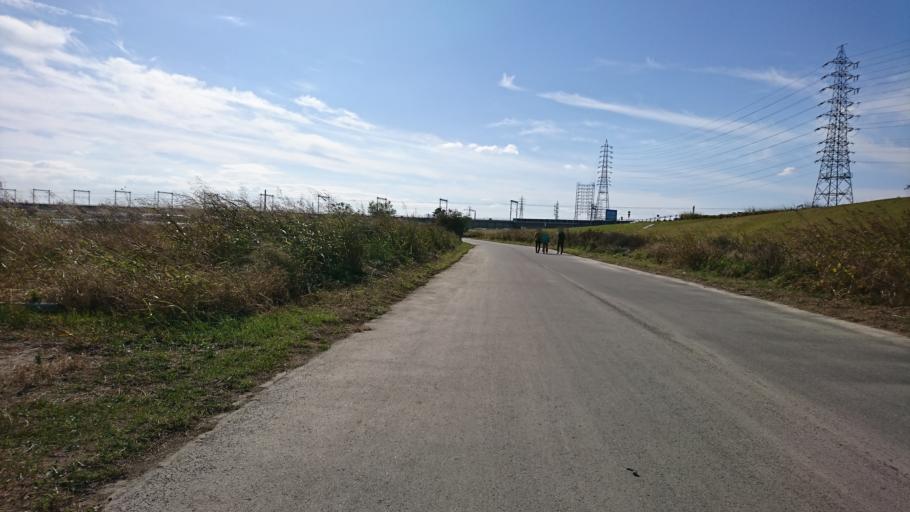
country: JP
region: Hyogo
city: Kakogawacho-honmachi
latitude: 34.7645
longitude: 134.8070
